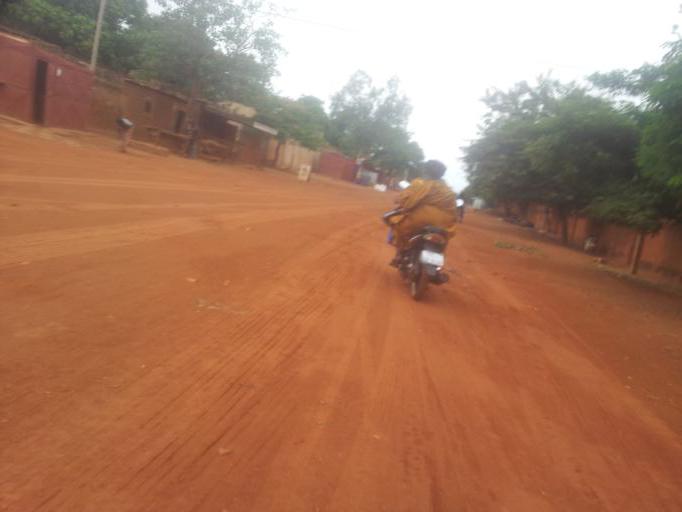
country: BF
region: Centre
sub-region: Kadiogo Province
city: Ouagadougou
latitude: 12.3814
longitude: -1.5451
